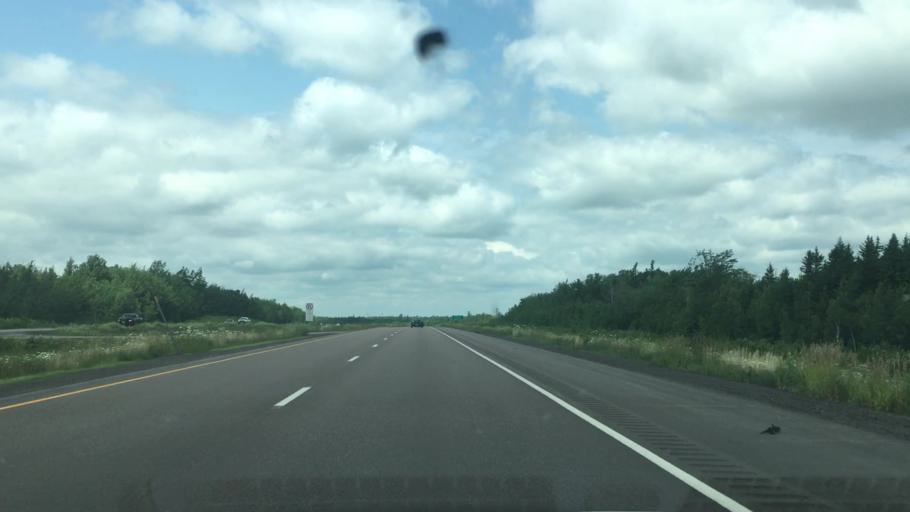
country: CA
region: New Brunswick
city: Dieppe
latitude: 46.1206
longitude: -64.6297
